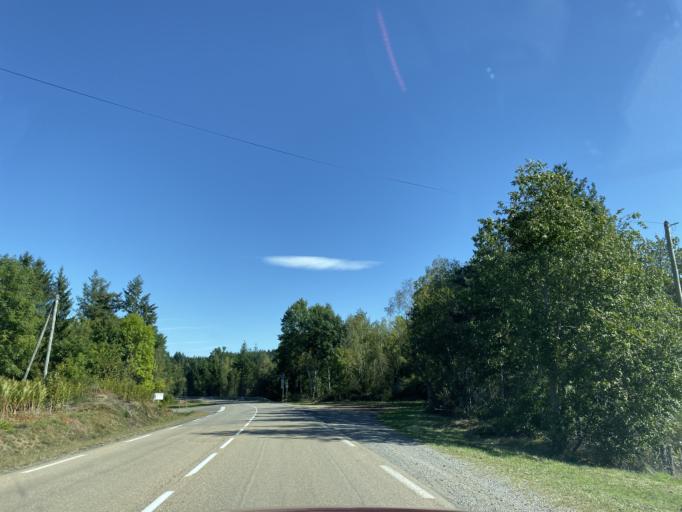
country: FR
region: Rhone-Alpes
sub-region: Departement de la Loire
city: Noiretable
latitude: 45.8328
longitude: 3.7843
